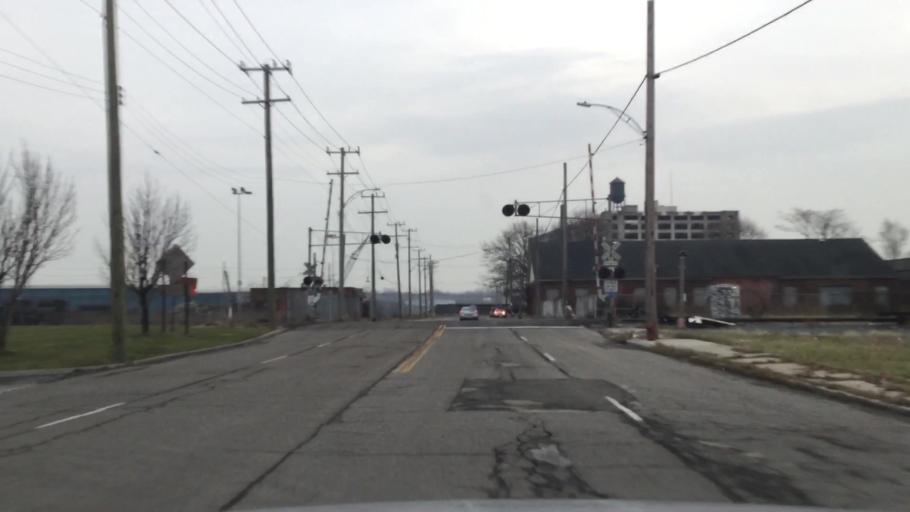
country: US
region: Michigan
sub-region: Wayne County
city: Detroit
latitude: 42.3101
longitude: -83.0886
